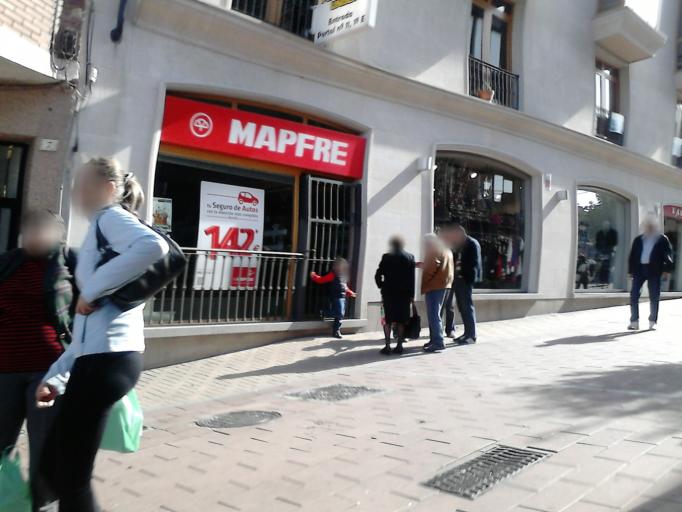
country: ES
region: Madrid
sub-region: Provincia de Madrid
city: Galapagar
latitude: 40.5769
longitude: -4.0034
